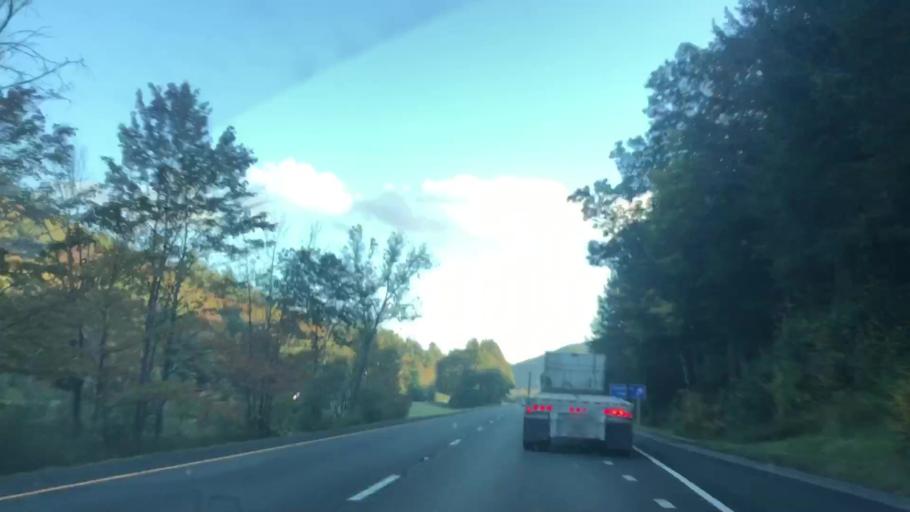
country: US
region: Massachusetts
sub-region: Franklin County
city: Bernardston
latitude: 42.7213
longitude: -72.5685
